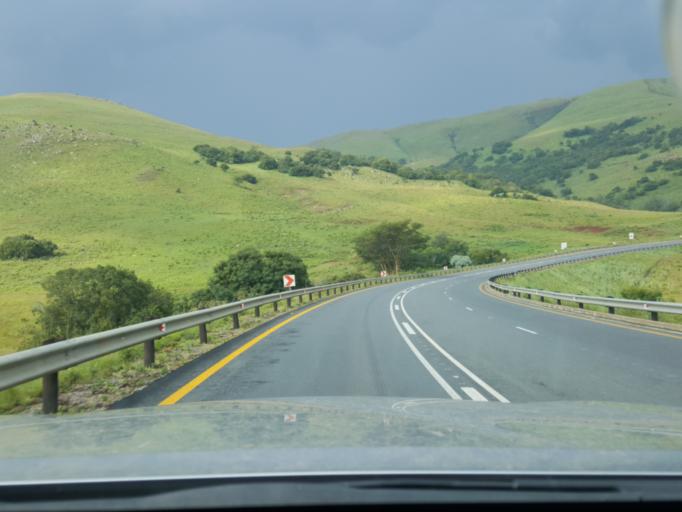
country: ZA
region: Mpumalanga
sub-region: Nkangala District Municipality
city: Belfast
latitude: -25.6269
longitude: 30.3279
